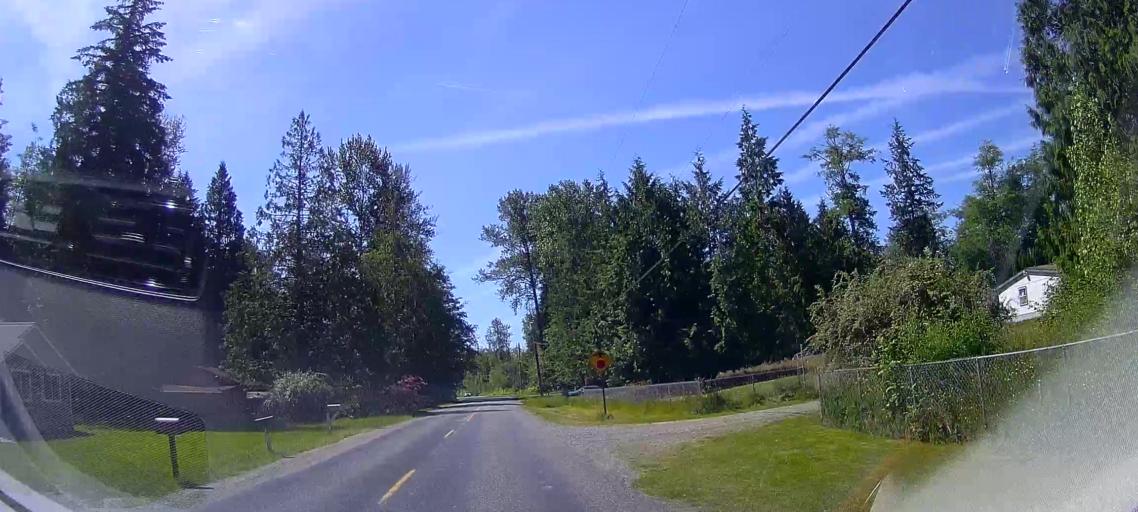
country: US
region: Washington
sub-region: Skagit County
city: Sedro-Woolley
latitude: 48.5443
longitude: -122.2483
